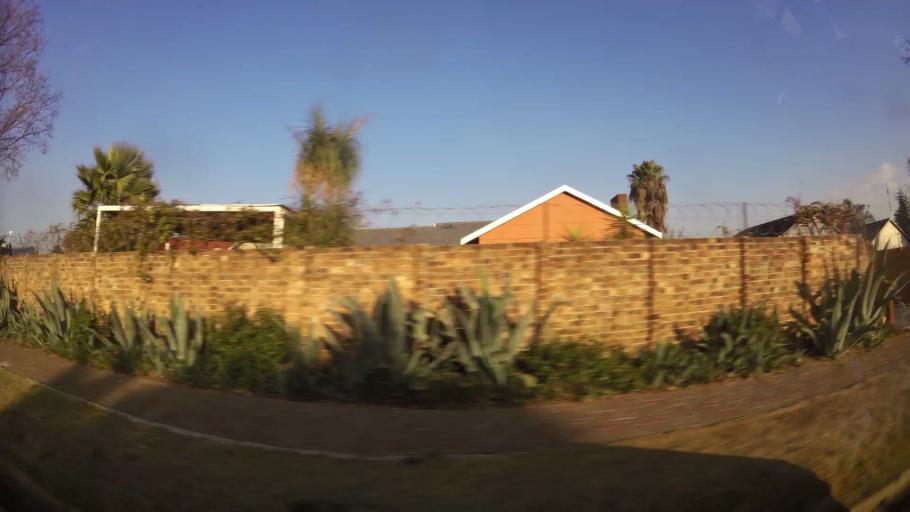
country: ZA
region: Gauteng
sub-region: Ekurhuleni Metropolitan Municipality
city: Germiston
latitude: -26.2652
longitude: 28.2292
